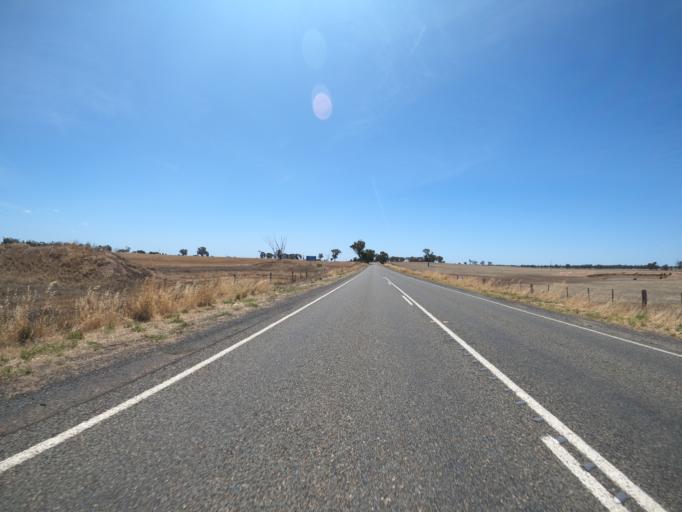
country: AU
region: Victoria
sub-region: Moira
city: Yarrawonga
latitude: -36.0953
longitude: 145.9955
